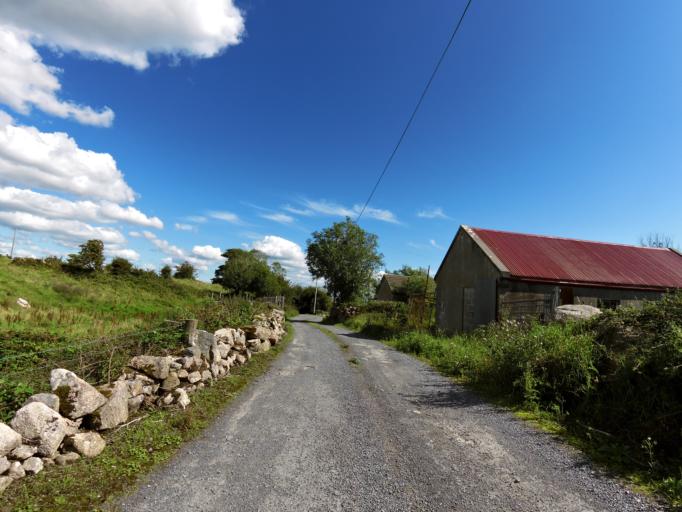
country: IE
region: Connaught
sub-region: County Galway
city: Gaillimh
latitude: 53.2859
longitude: -9.0916
